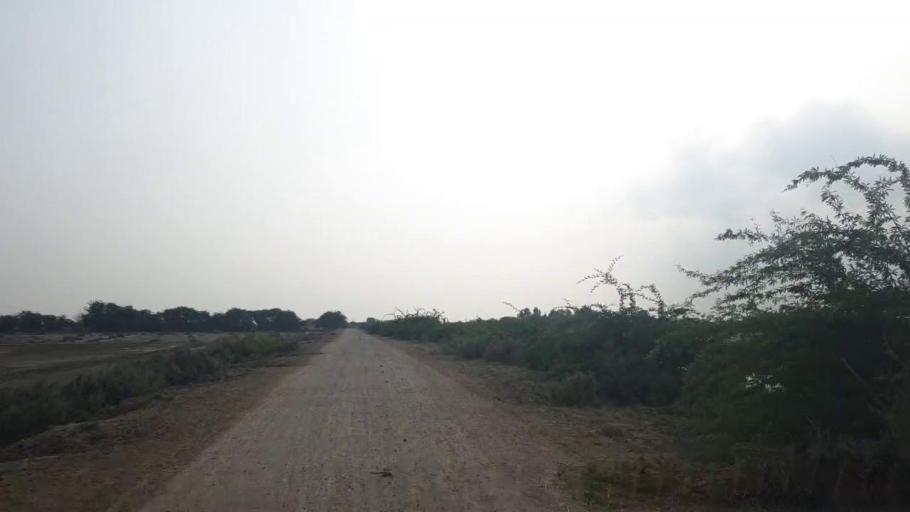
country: PK
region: Sindh
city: Badin
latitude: 24.6284
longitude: 68.6919
